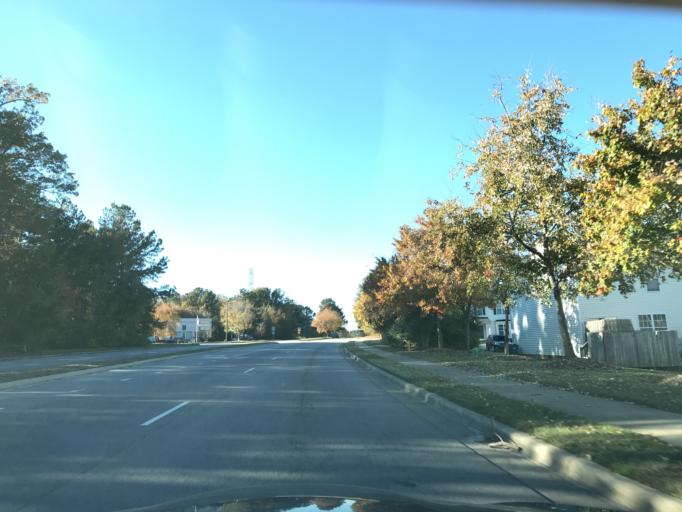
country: US
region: North Carolina
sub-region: Wake County
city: Garner
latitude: 35.7622
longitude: -78.5547
